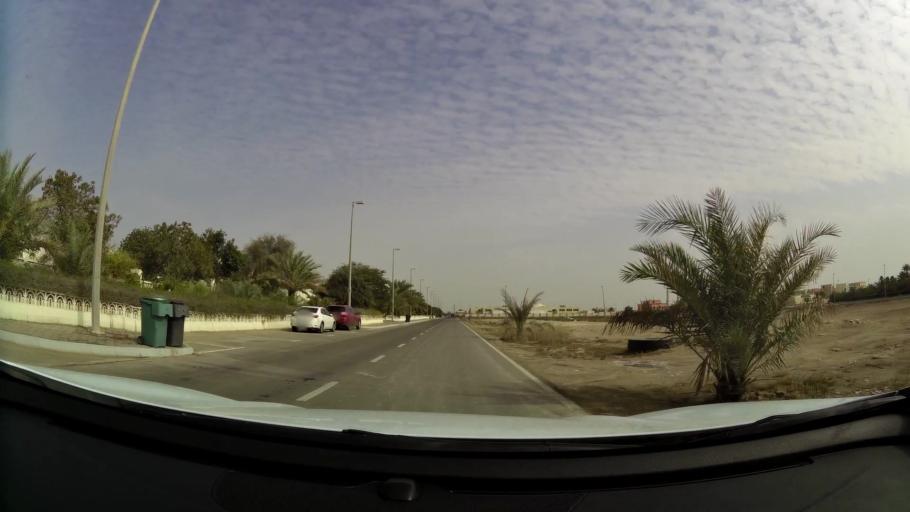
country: AE
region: Abu Dhabi
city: Abu Dhabi
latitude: 24.5977
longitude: 54.6965
